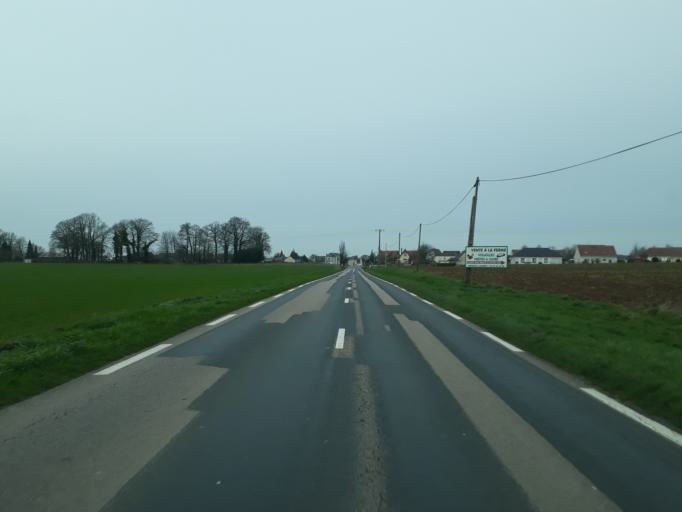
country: FR
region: Haute-Normandie
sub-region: Departement de la Seine-Maritime
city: Breaute
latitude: 49.6222
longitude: 0.4023
